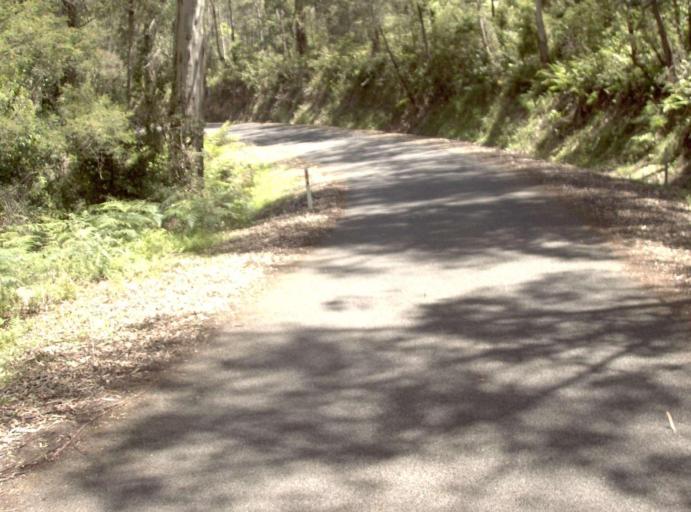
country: AU
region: New South Wales
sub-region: Bombala
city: Bombala
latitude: -37.4420
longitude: 148.9513
